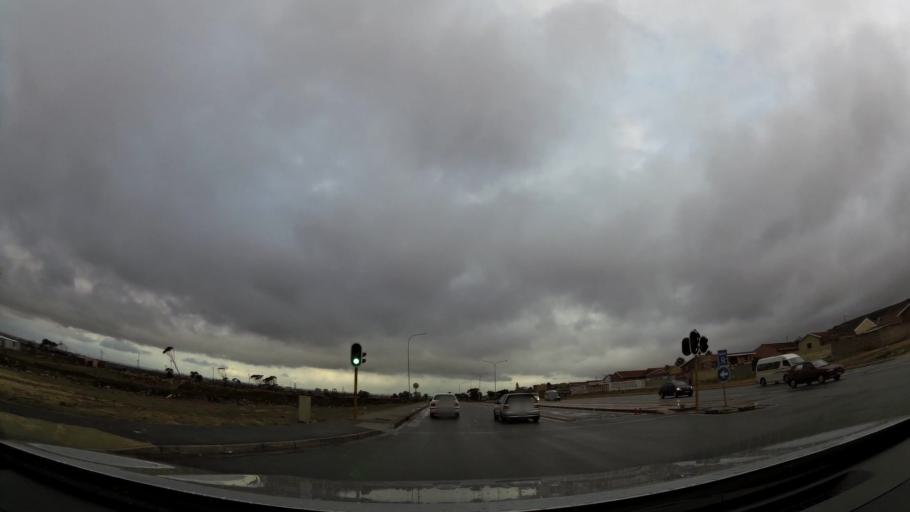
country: ZA
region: Eastern Cape
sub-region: Nelson Mandela Bay Metropolitan Municipality
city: Port Elizabeth
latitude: -33.8949
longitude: 25.5315
